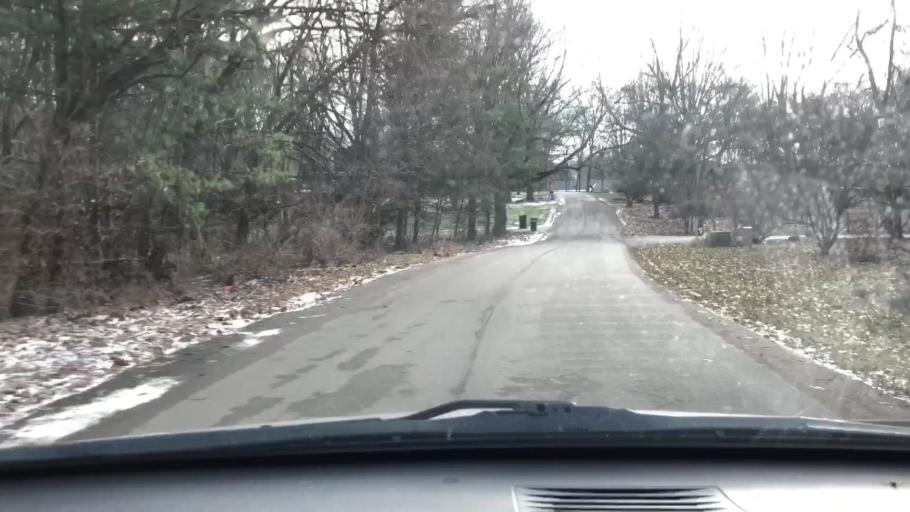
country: US
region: Indiana
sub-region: Steuben County
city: Angola
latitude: 41.6825
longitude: -85.0056
